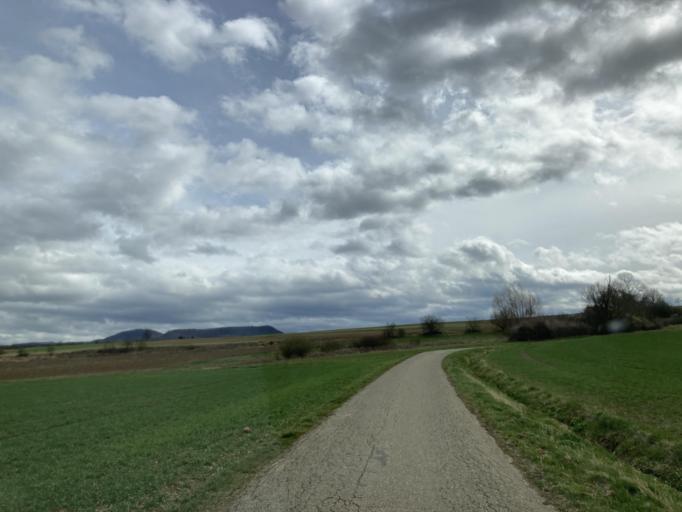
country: DE
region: Baden-Wuerttemberg
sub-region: Tuebingen Region
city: Gomaringen
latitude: 48.4707
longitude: 9.1008
